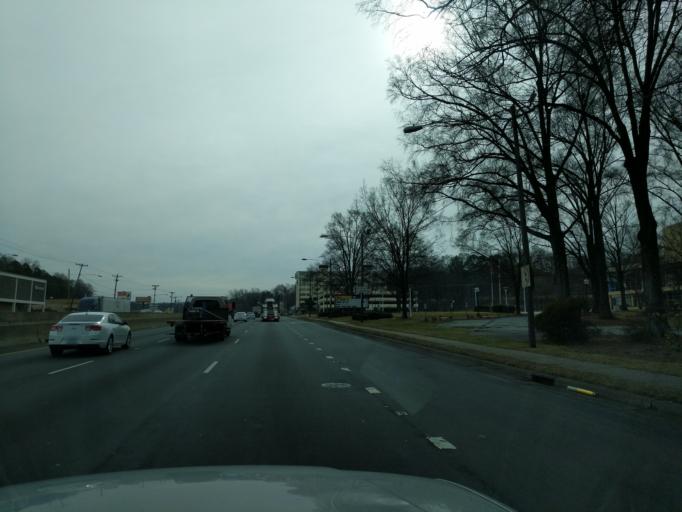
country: US
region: North Carolina
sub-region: Mecklenburg County
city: Charlotte
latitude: 35.2059
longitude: -80.7950
